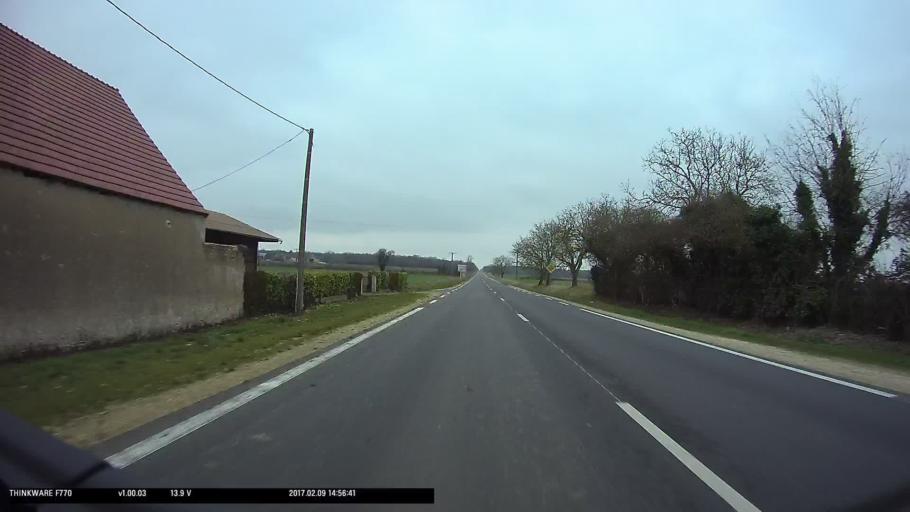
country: FR
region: Centre
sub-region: Departement du Cher
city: Levet
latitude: 46.8627
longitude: 2.4191
